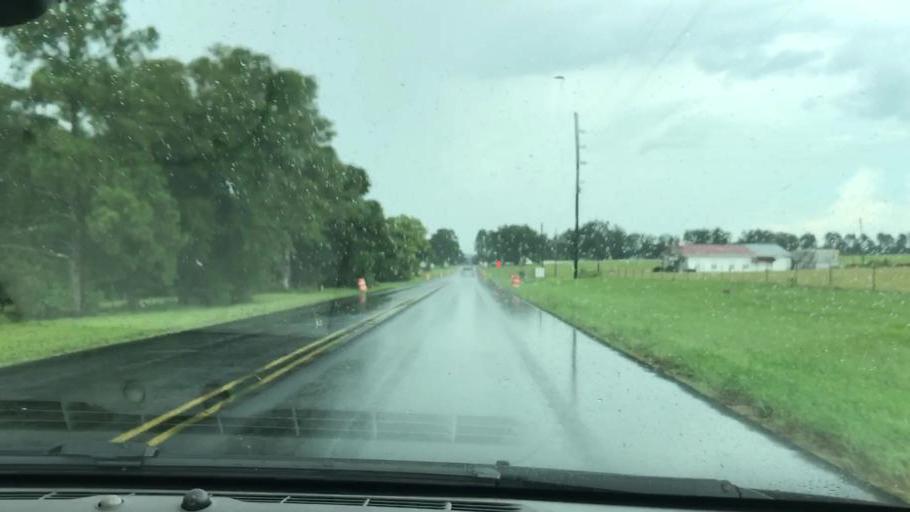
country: US
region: Georgia
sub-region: Clay County
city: Fort Gaines
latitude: 31.5386
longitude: -85.0210
